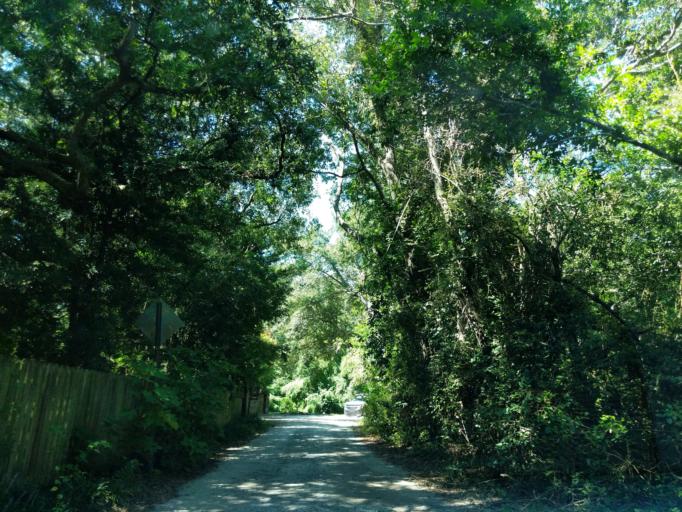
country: US
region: South Carolina
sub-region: Charleston County
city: Folly Beach
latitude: 32.7060
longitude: -79.9392
